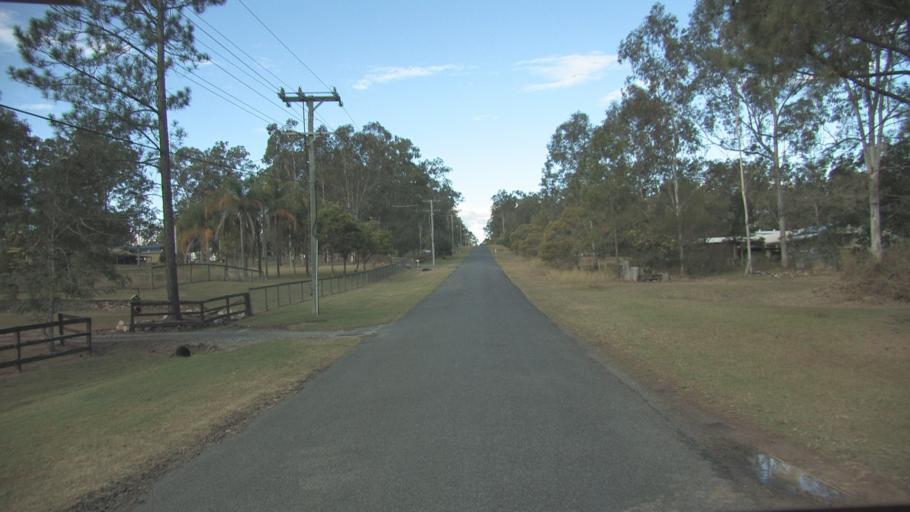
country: AU
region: Queensland
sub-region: Logan
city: North Maclean
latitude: -27.8181
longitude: 153.0494
